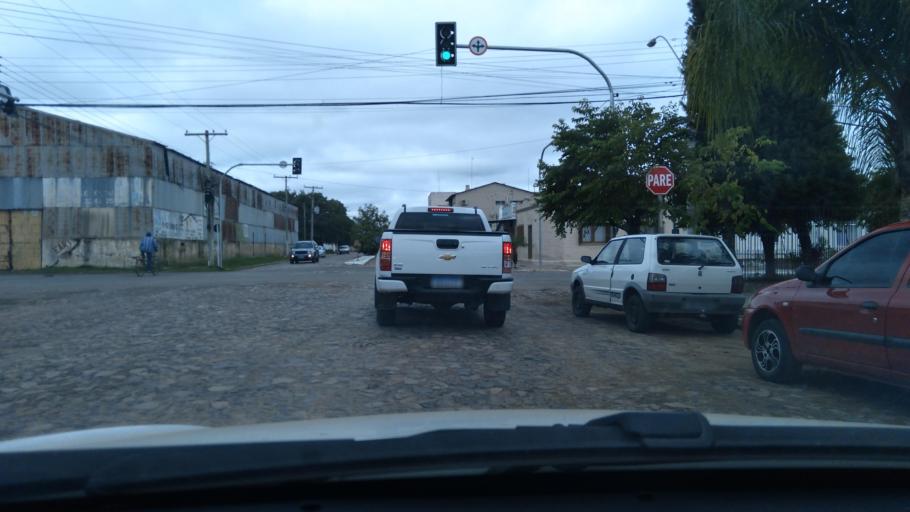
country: BR
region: Rio Grande do Sul
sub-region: Dom Pedrito
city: Dom Pedrito
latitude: -30.9741
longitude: -54.6745
